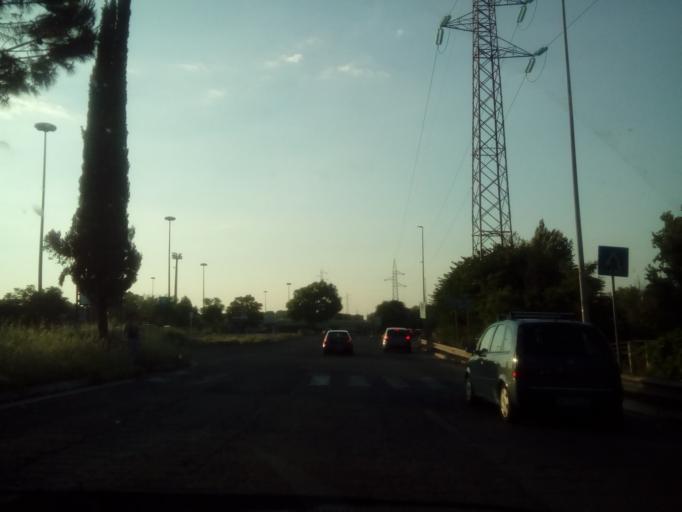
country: IT
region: Latium
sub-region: Citta metropolitana di Roma Capitale
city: Rome
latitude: 41.9187
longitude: 12.5678
